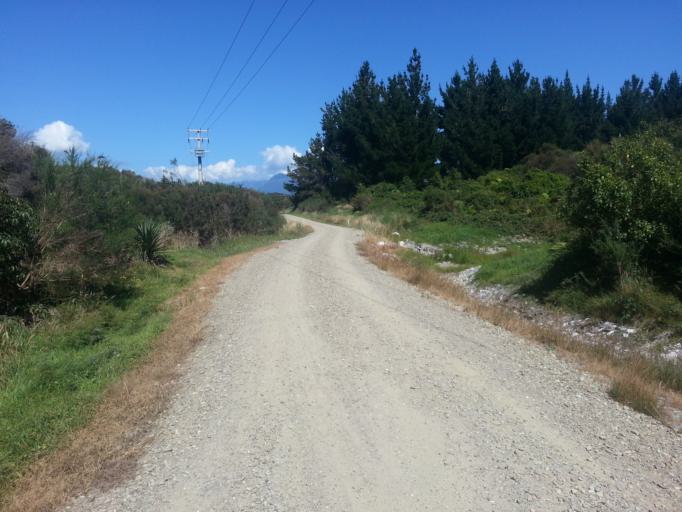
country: NZ
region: West Coast
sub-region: Grey District
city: Greymouth
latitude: -42.6257
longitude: 171.1848
